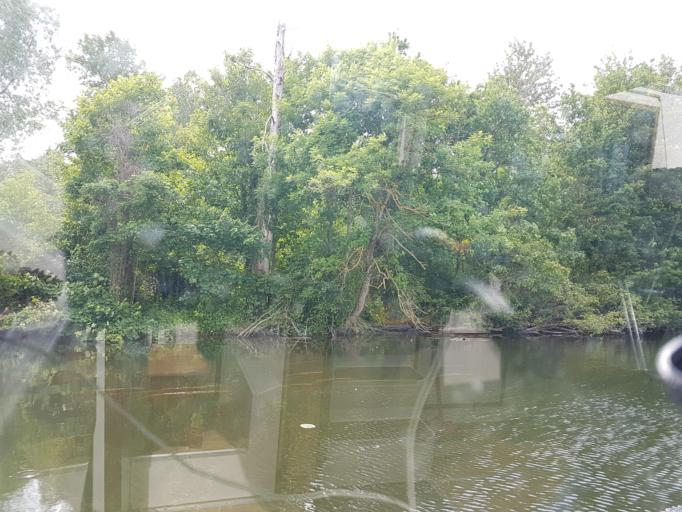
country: FR
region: Bourgogne
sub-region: Departement de l'Yonne
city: Gurgy
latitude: 47.8571
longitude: 3.5567
